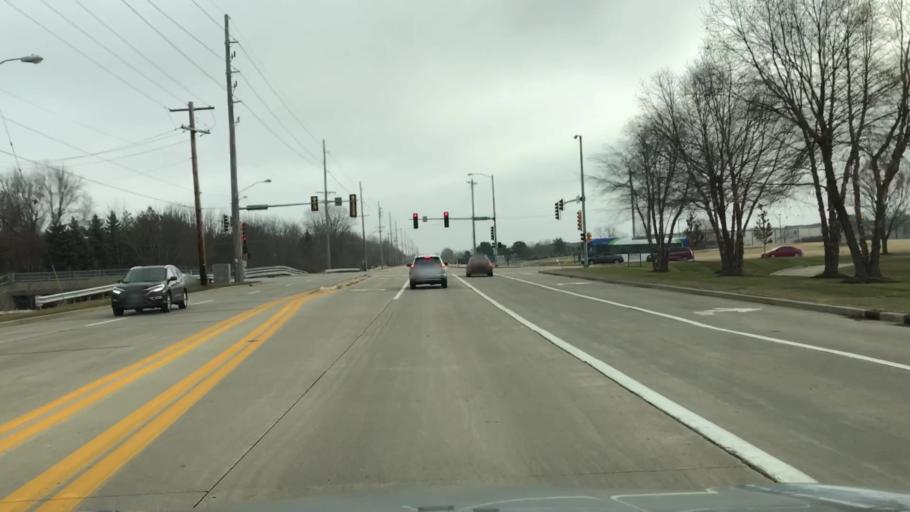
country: US
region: Illinois
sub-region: McLean County
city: Normal
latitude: 40.5027
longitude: -88.9398
